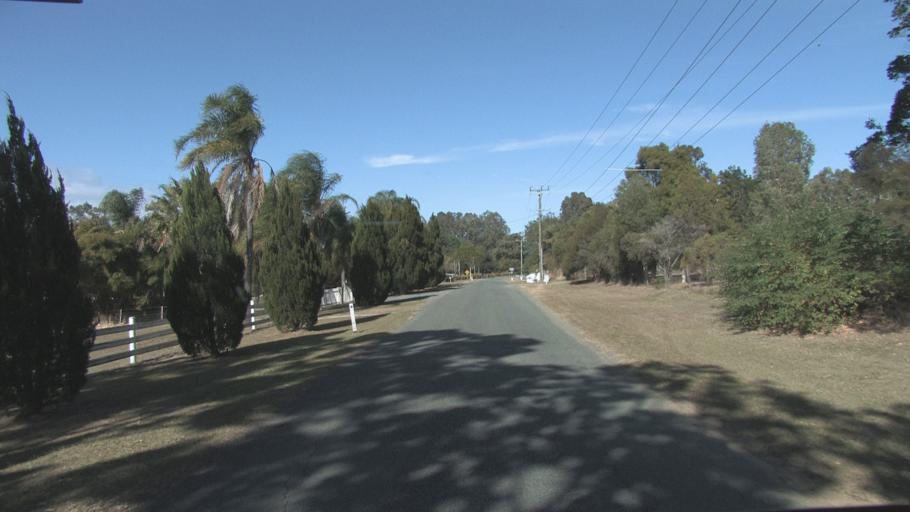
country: AU
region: Queensland
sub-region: Logan
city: Cedar Vale
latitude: -27.8583
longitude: 152.9763
